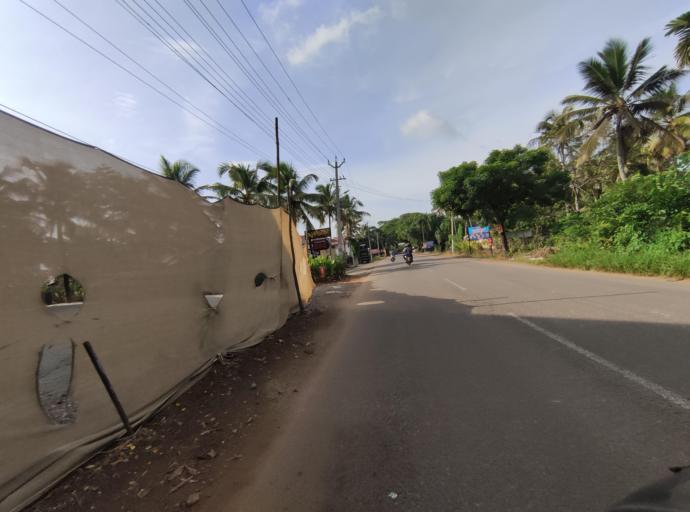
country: IN
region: Kerala
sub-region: Alappuzha
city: Shertallai
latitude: 9.6307
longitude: 76.4300
